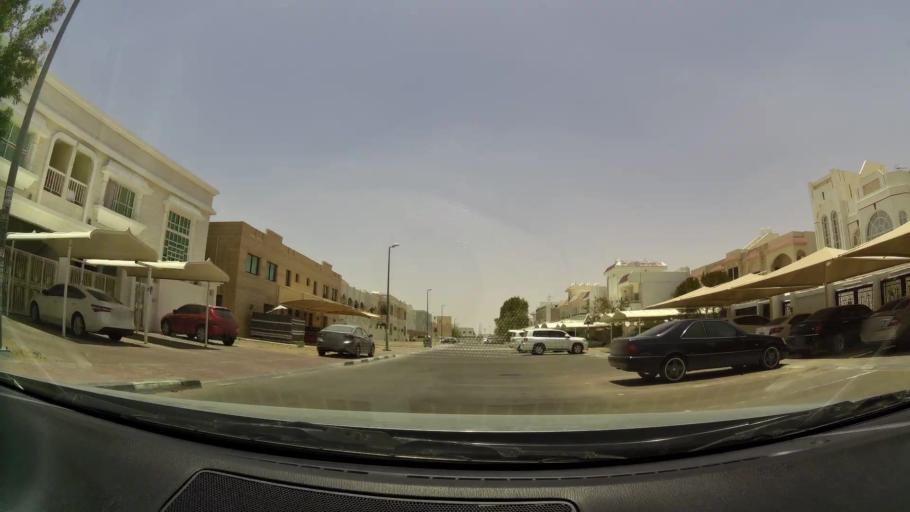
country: OM
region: Al Buraimi
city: Al Buraymi
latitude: 24.2617
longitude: 55.7243
